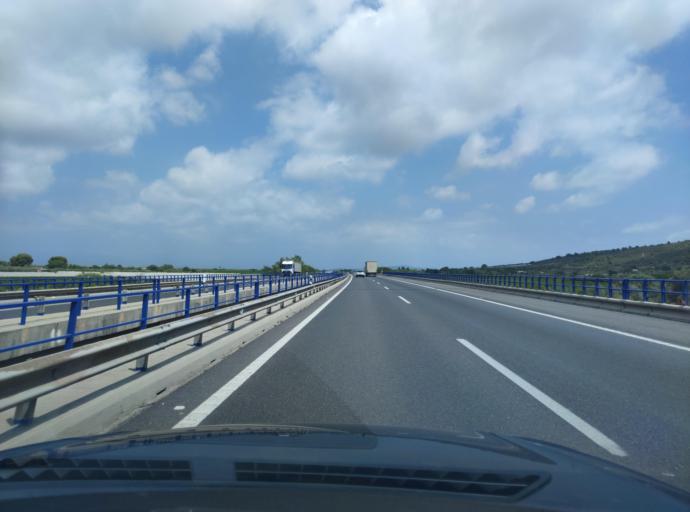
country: ES
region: Valencia
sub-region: Provincia de Castello
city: Vinaros
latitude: 40.5011
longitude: 0.4160
